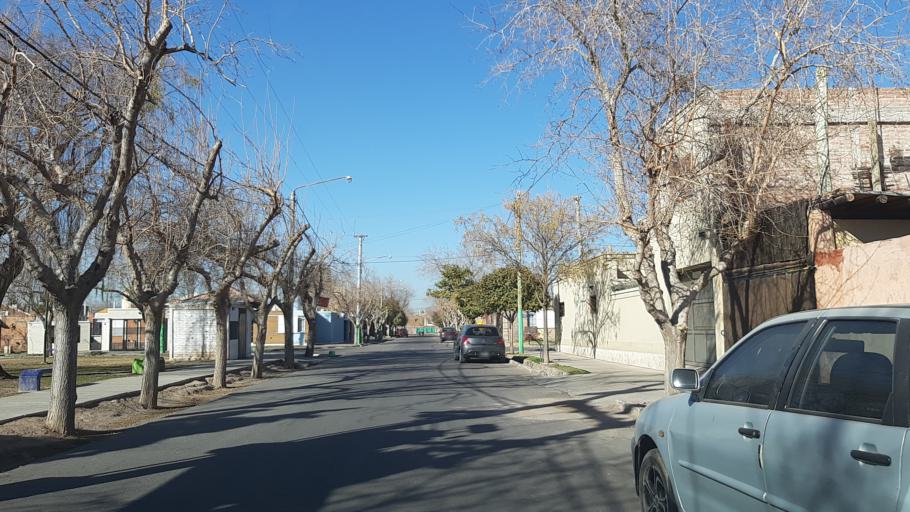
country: AR
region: San Juan
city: Villa Paula de Sarmiento
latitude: -31.5171
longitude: -68.5898
